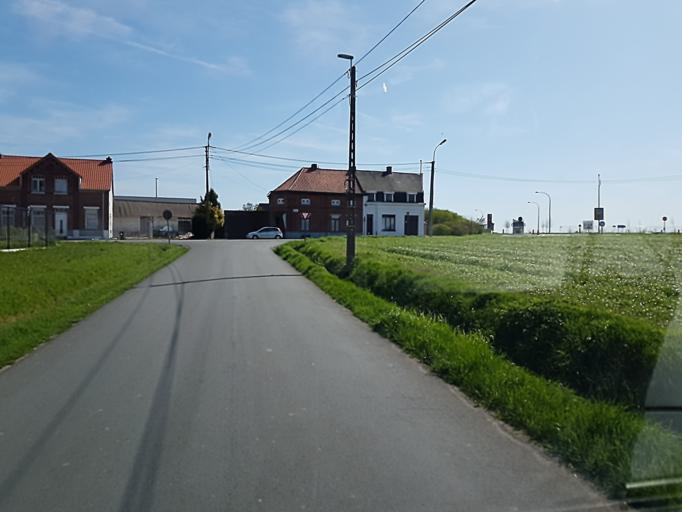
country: BE
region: Flanders
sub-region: Provincie Oost-Vlaanderen
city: Ronse
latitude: 50.7413
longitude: 3.5757
